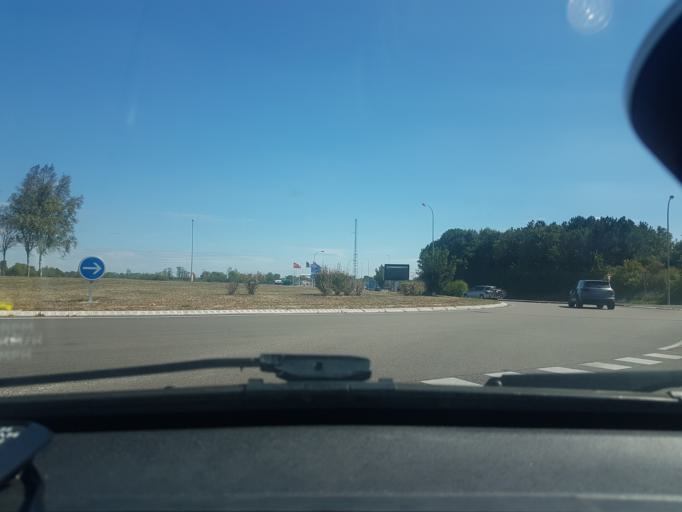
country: FR
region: Bourgogne
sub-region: Departement de la Cote-d'Or
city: Couternon
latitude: 47.3447
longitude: 5.1556
